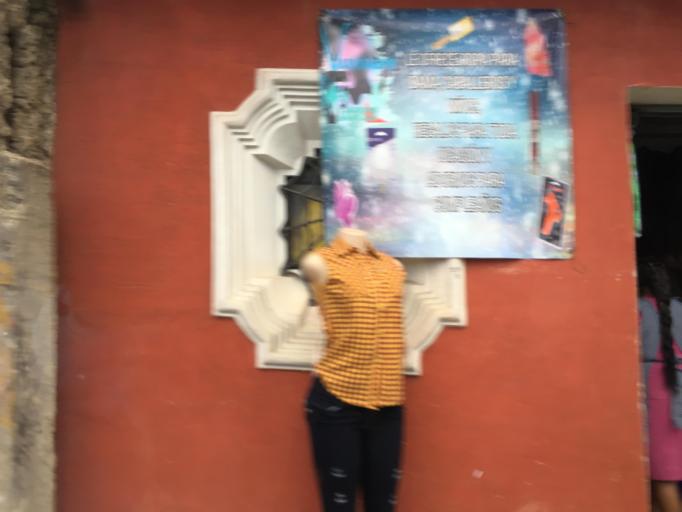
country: GT
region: Sacatepequez
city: Ciudad Vieja
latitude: 14.5253
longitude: -90.7518
